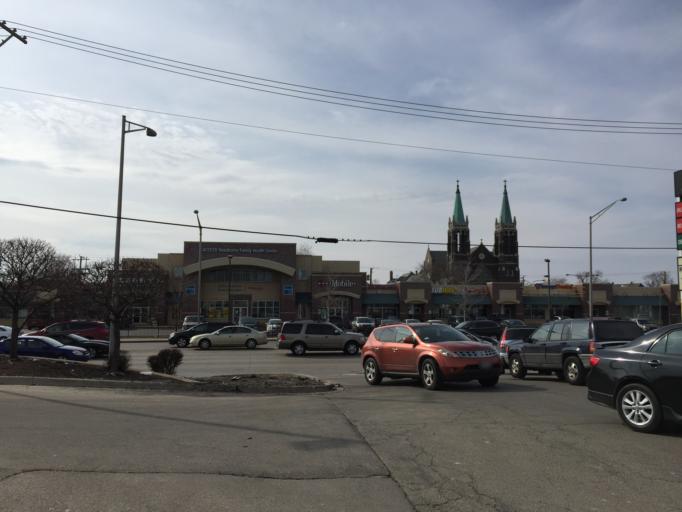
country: US
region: Illinois
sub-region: Cook County
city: Cicero
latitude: 41.8377
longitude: -87.7433
